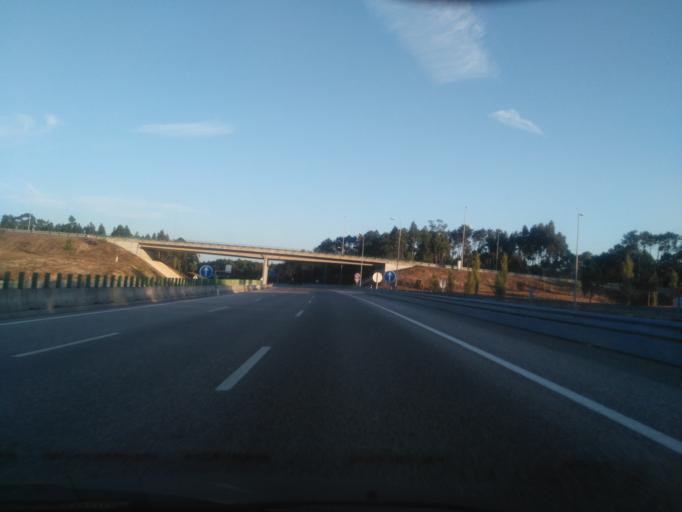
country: PT
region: Leiria
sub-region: Pombal
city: Lourical
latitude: 39.9904
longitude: -8.7964
